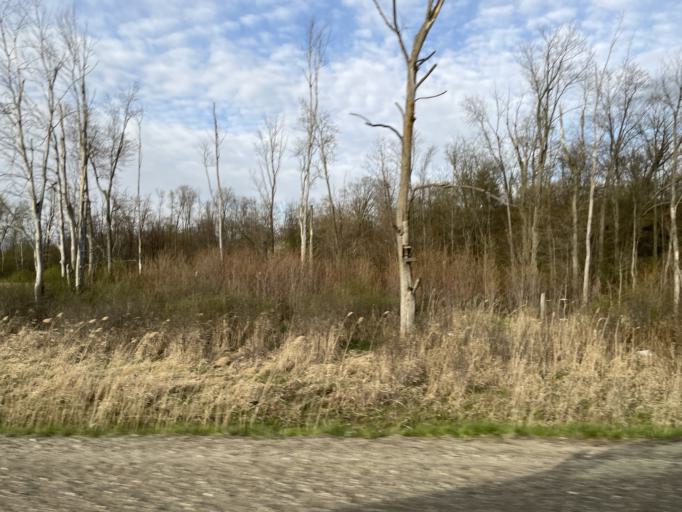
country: CA
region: Ontario
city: Waterloo
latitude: 43.4778
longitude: -80.4036
